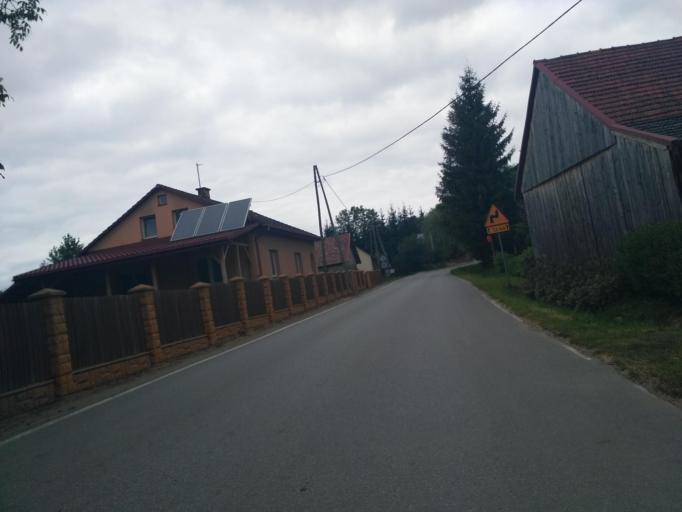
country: PL
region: Subcarpathian Voivodeship
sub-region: Powiat krosnienski
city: Wojaszowka
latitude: 49.7742
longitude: 21.6880
